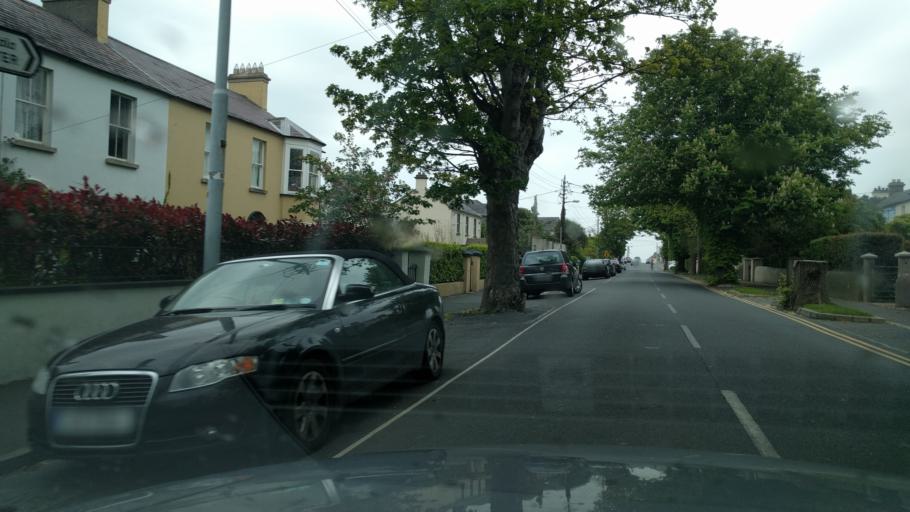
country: IE
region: Leinster
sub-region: Wicklow
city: Greystones
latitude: 53.1469
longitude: -6.0672
